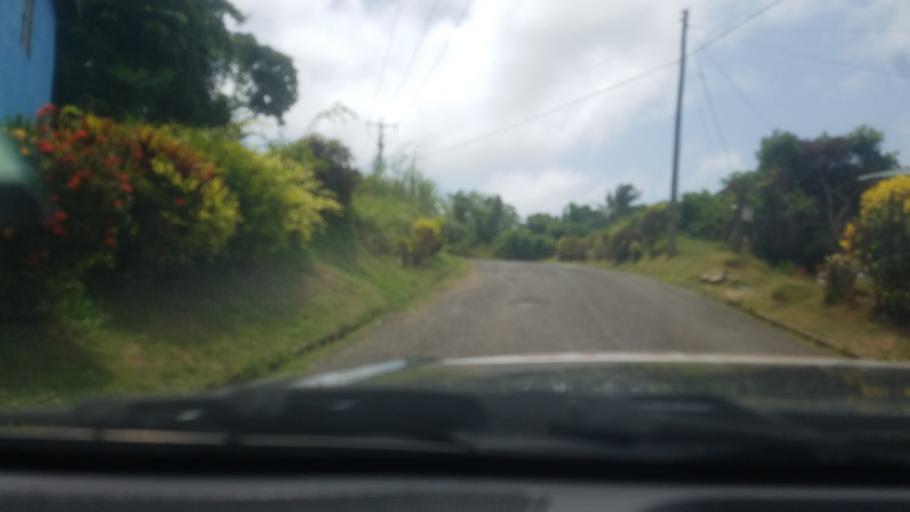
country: LC
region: Laborie Quarter
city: Laborie
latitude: 13.7908
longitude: -60.9531
